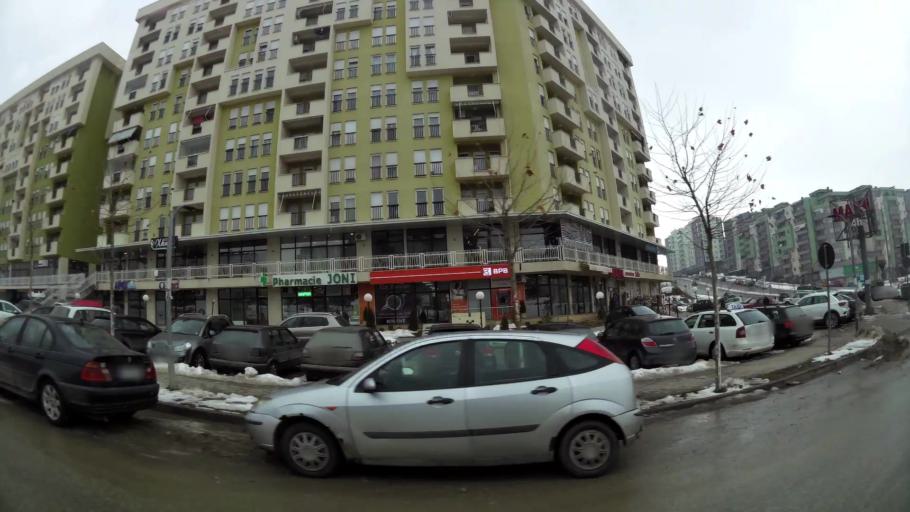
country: XK
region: Pristina
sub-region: Komuna e Prishtines
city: Pristina
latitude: 42.6529
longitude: 21.1759
